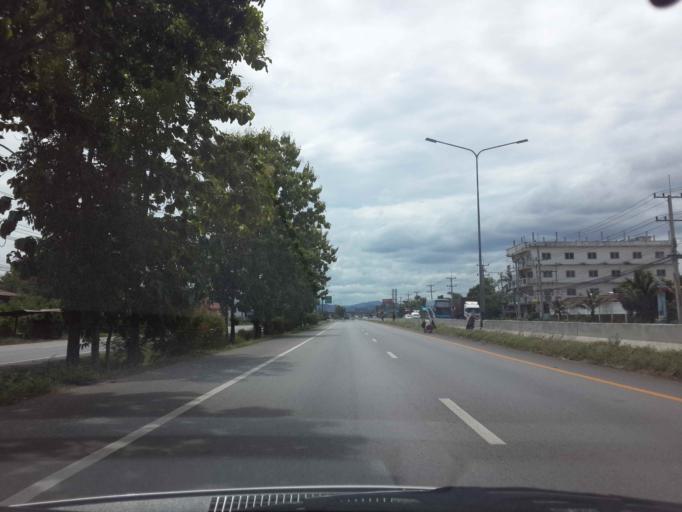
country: TH
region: Phetchaburi
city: Phetchaburi
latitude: 13.1187
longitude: 99.9029
